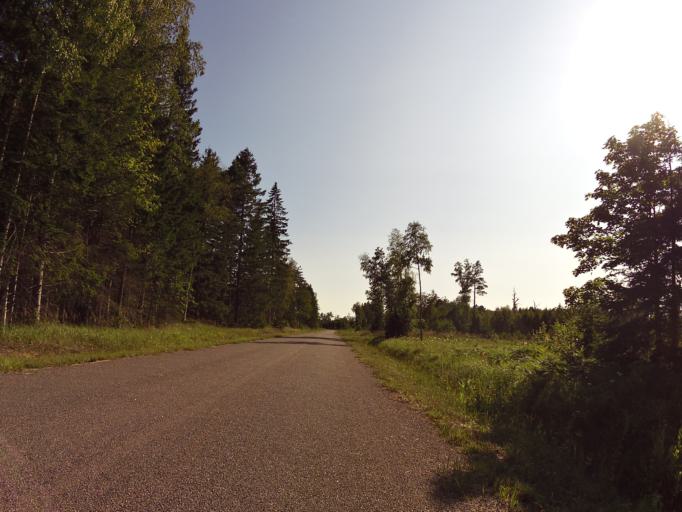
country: EE
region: Hiiumaa
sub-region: Kaerdla linn
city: Kardla
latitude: 58.9042
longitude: 22.2844
